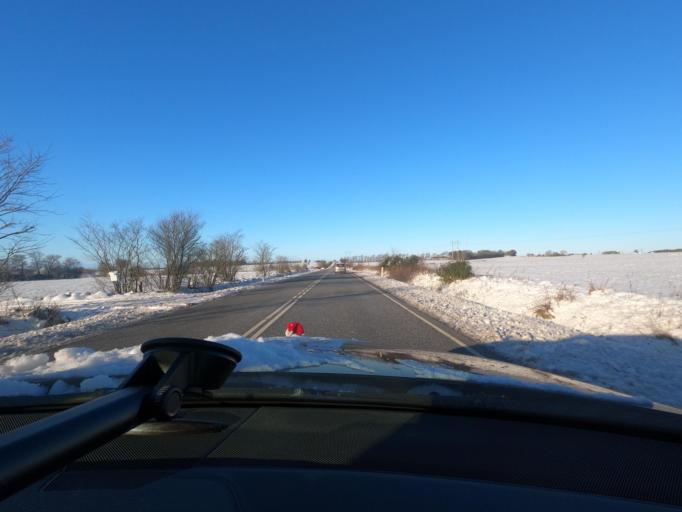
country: DK
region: South Denmark
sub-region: Aabenraa Kommune
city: Rodekro
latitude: 55.0963
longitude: 9.1931
